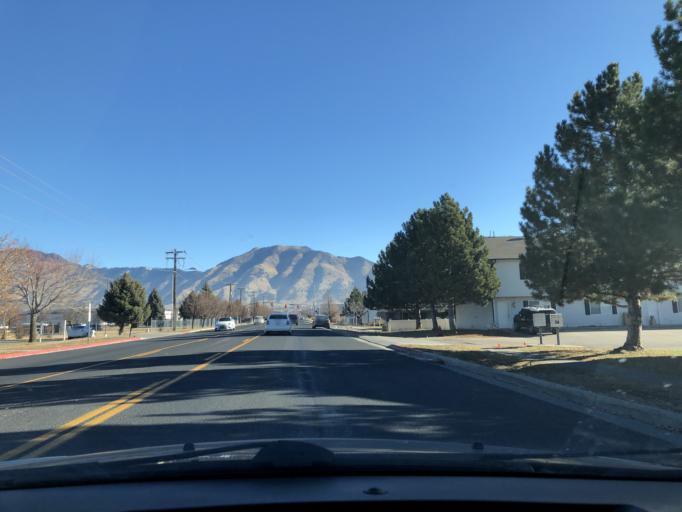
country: US
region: Utah
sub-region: Cache County
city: Logan
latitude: 41.7577
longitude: -111.8416
